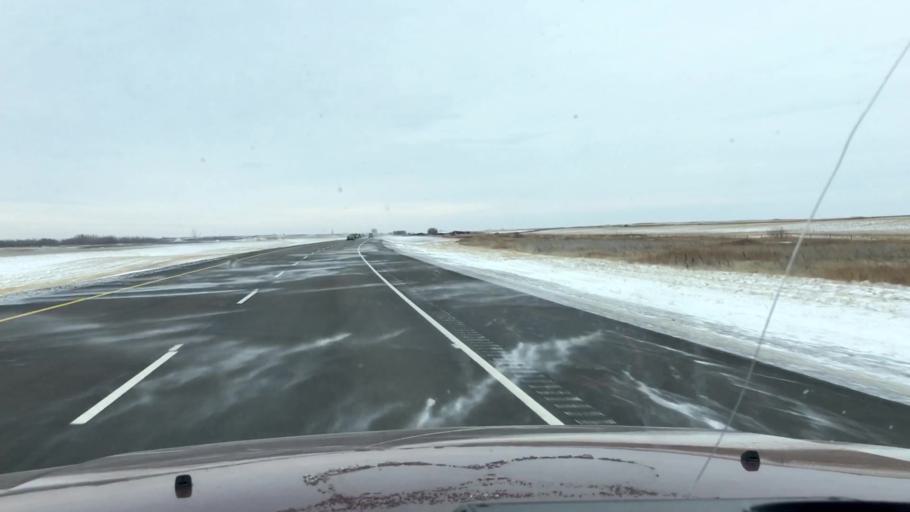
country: CA
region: Saskatchewan
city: Moose Jaw
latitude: 50.8971
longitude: -105.6308
